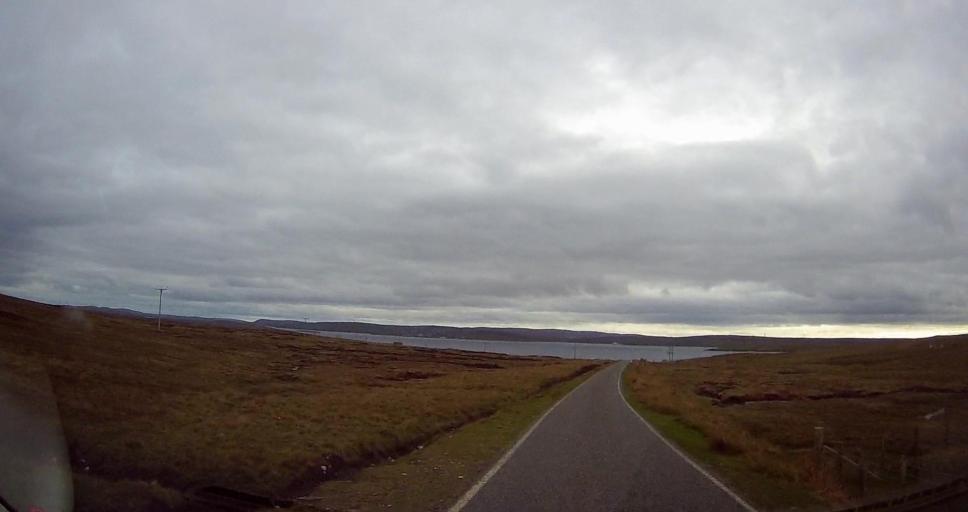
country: GB
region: Scotland
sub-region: Shetland Islands
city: Shetland
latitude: 60.5023
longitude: -1.1490
